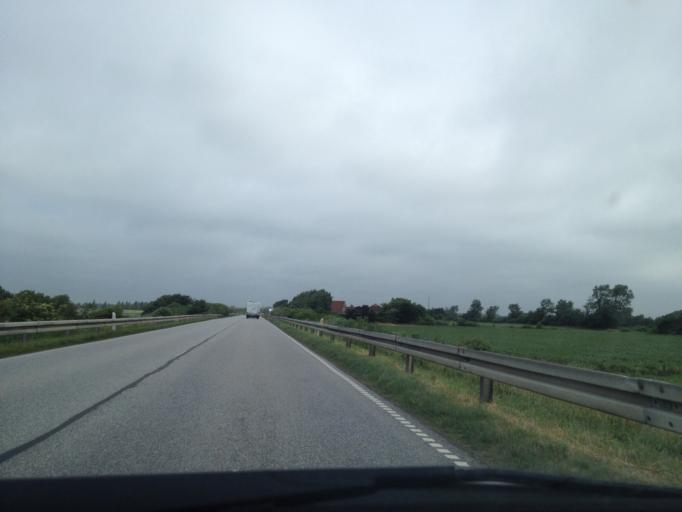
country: DK
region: South Denmark
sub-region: Tonder Kommune
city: Sherrebek
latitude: 55.2393
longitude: 8.7238
